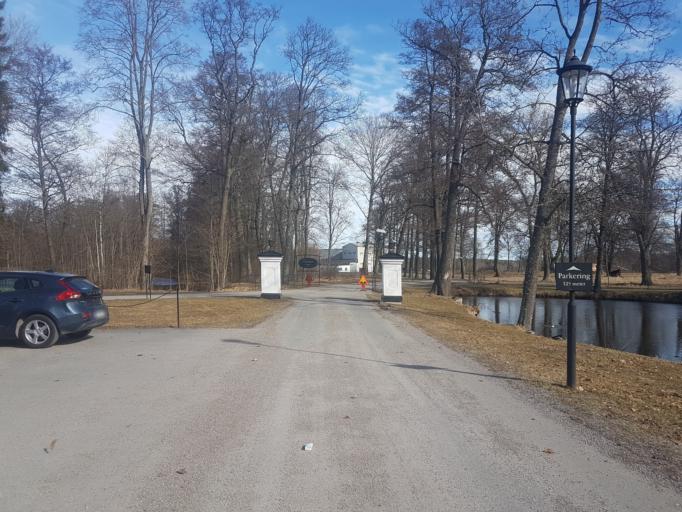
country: SE
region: Stockholm
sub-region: Norrtalje Kommun
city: Nykvarn
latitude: 59.7916
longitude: 18.2960
